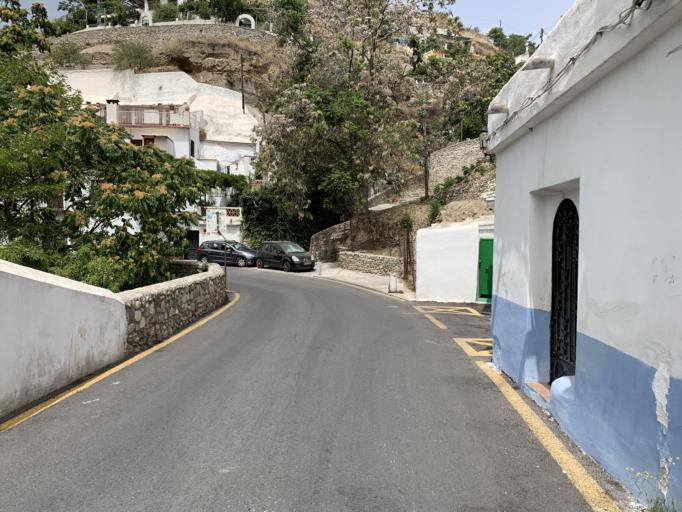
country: ES
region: Andalusia
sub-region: Provincia de Granada
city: Granada
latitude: 37.1818
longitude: -3.5845
